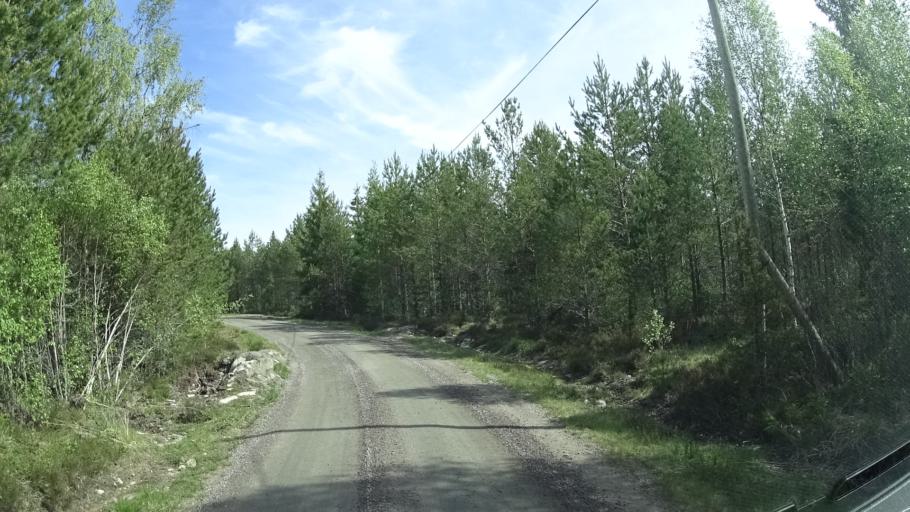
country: SE
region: OEstergoetland
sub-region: Finspangs Kommun
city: Finspang
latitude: 58.7737
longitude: 15.8531
